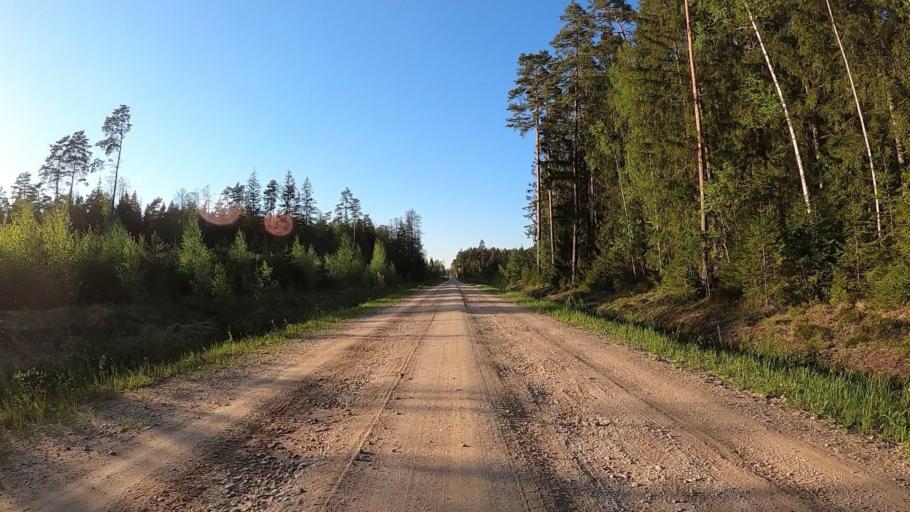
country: LV
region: Kekava
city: Kekava
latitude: 56.7631
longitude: 24.2227
